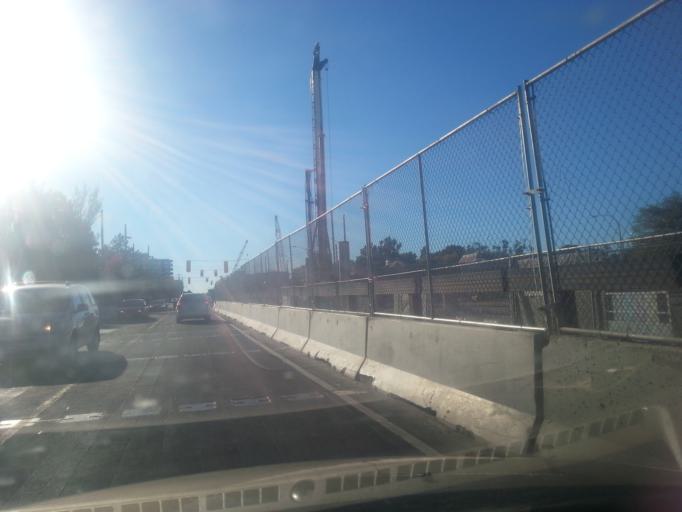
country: CA
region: Ontario
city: Toronto
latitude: 43.6991
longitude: -79.4343
